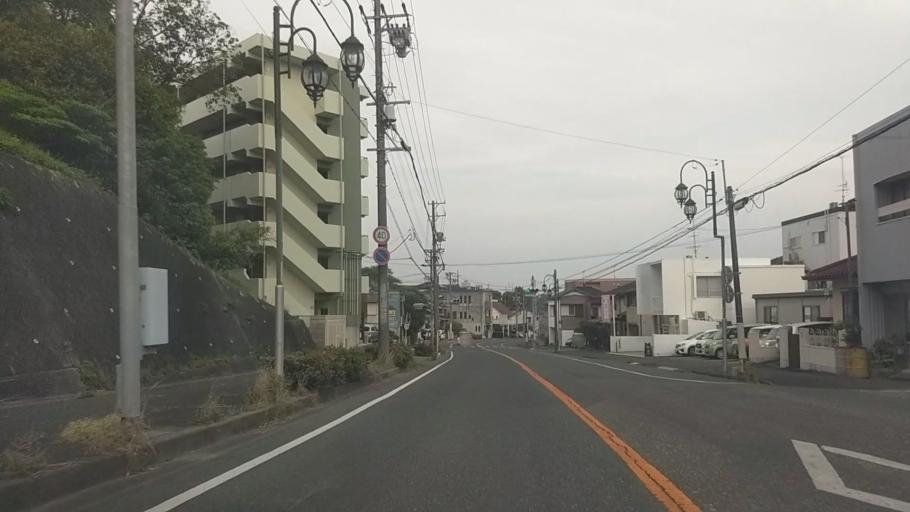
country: JP
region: Shizuoka
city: Hamamatsu
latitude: 34.7274
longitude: 137.6918
